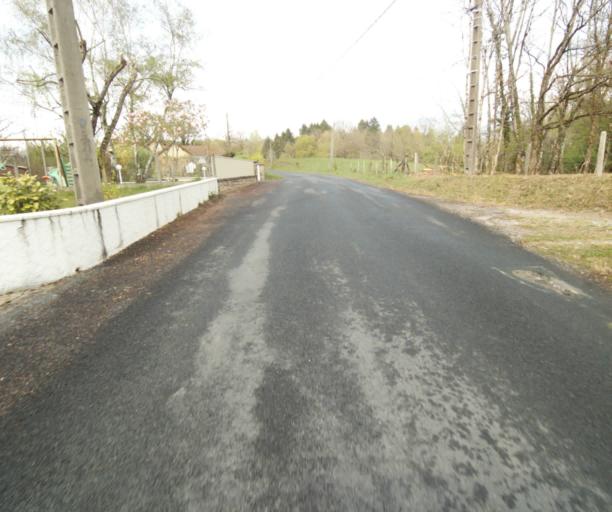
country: FR
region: Limousin
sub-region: Departement de la Correze
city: Tulle
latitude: 45.2680
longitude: 1.7504
